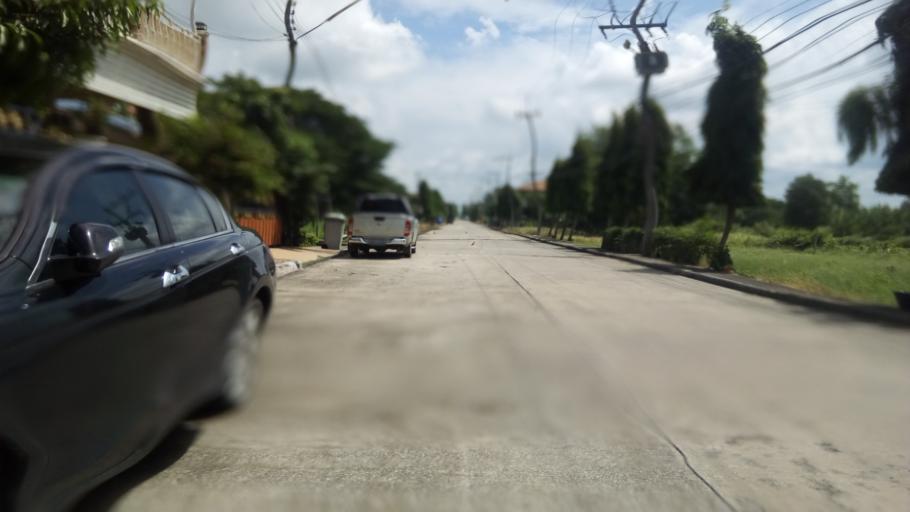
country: TH
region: Pathum Thani
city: Nong Suea
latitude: 14.0597
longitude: 100.8604
